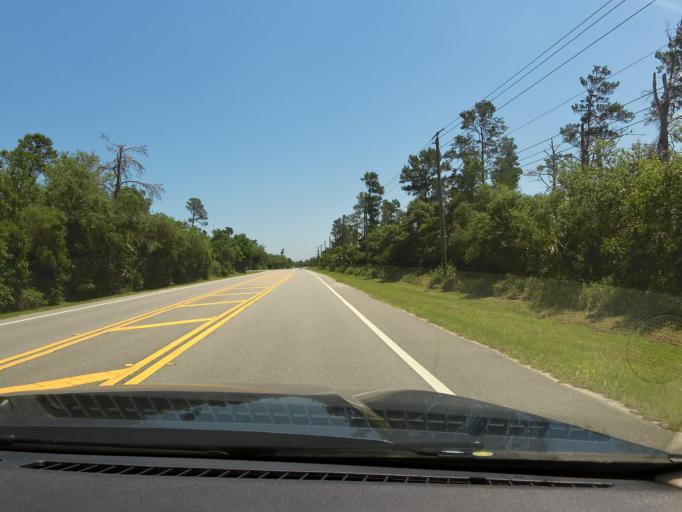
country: US
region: Florida
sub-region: Flagler County
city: Flagler Beach
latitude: 29.4407
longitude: -81.1597
